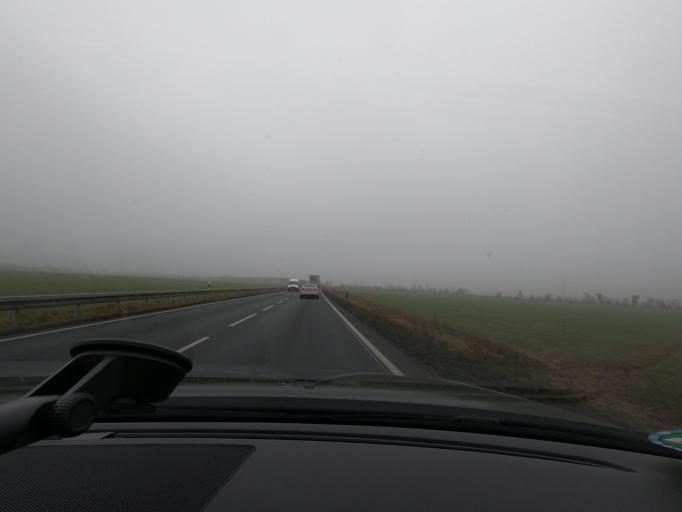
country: DE
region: North Rhine-Westphalia
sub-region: Regierungsbezirk Koln
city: Merzenich
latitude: 50.7992
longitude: 6.5228
